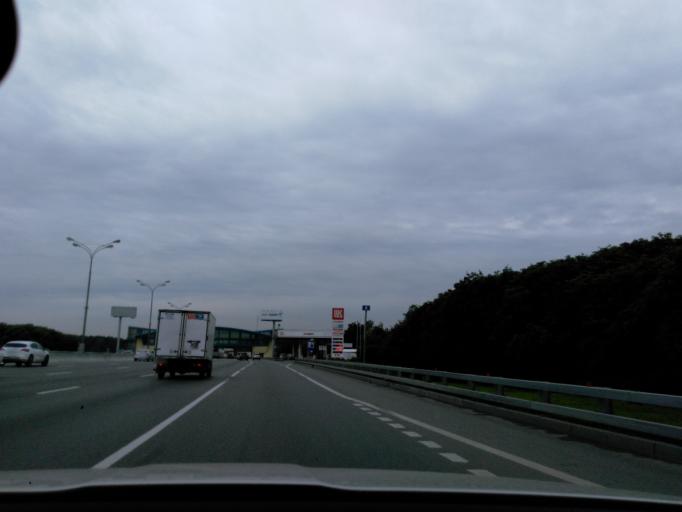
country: RU
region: Moscow
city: Vykhino-Zhulebino
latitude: 55.6991
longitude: 37.8302
